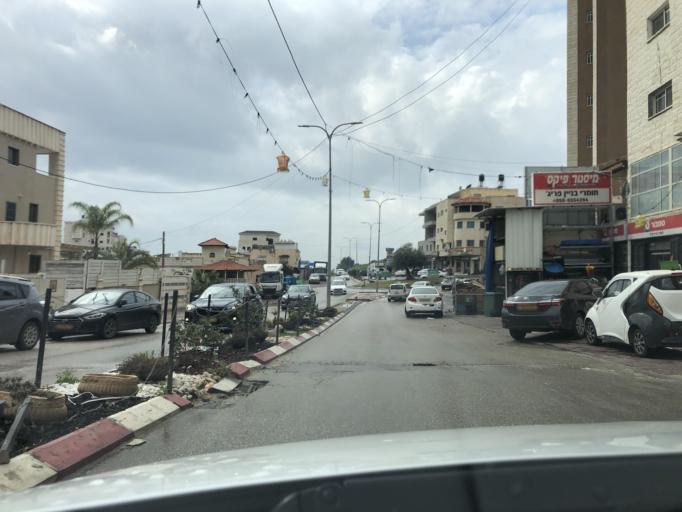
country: IL
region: Central District
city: Kafr Qasim
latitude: 32.1115
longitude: 34.9691
